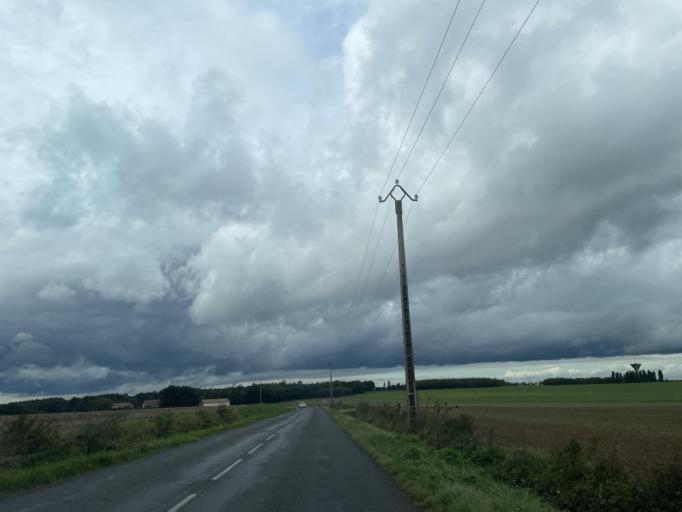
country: FR
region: Ile-de-France
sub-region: Departement de Seine-et-Marne
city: Saint-Jean-les-Deux-Jumeaux
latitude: 48.9303
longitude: 2.9963
